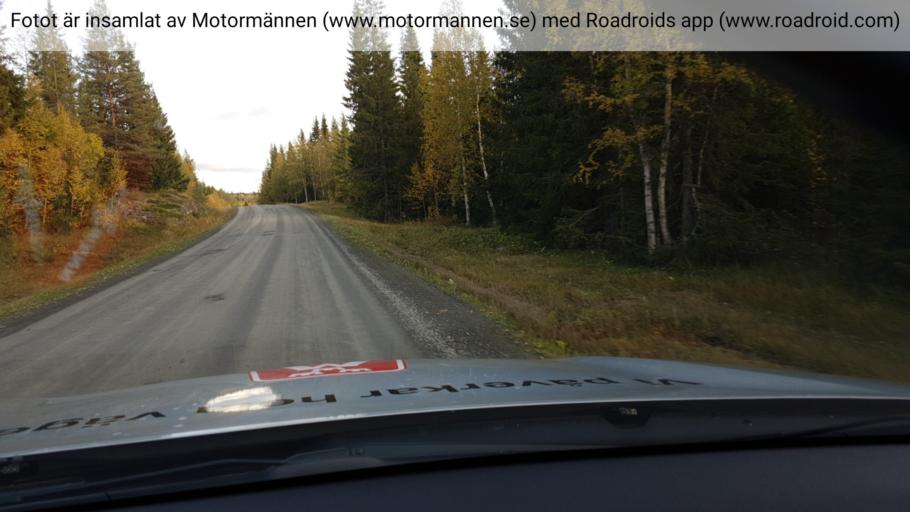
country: SE
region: Jaemtland
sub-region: Krokoms Kommun
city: Krokom
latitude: 63.7403
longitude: 14.4745
